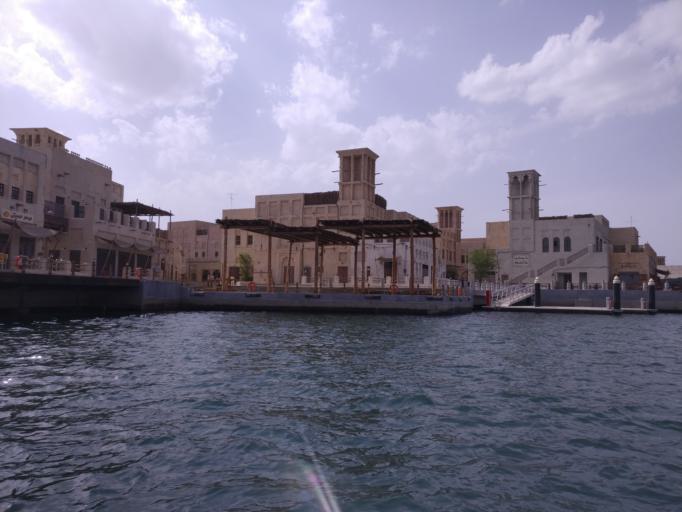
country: AE
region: Ash Shariqah
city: Sharjah
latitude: 25.2639
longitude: 55.3069
